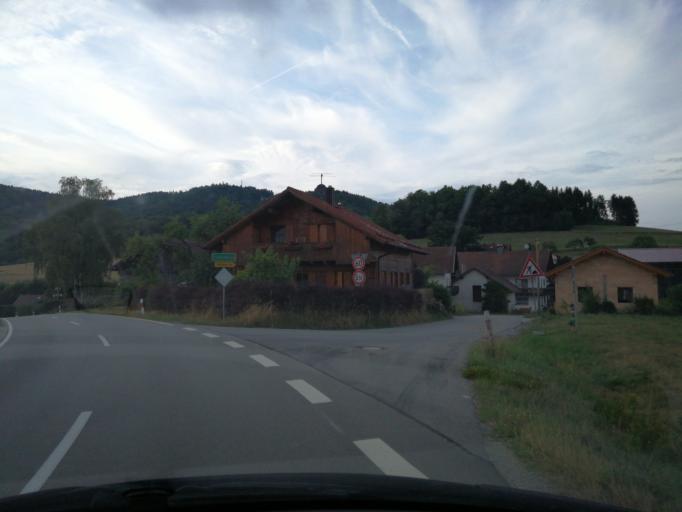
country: DE
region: Bavaria
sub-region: Lower Bavaria
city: Haibach
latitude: 49.0353
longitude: 12.7014
